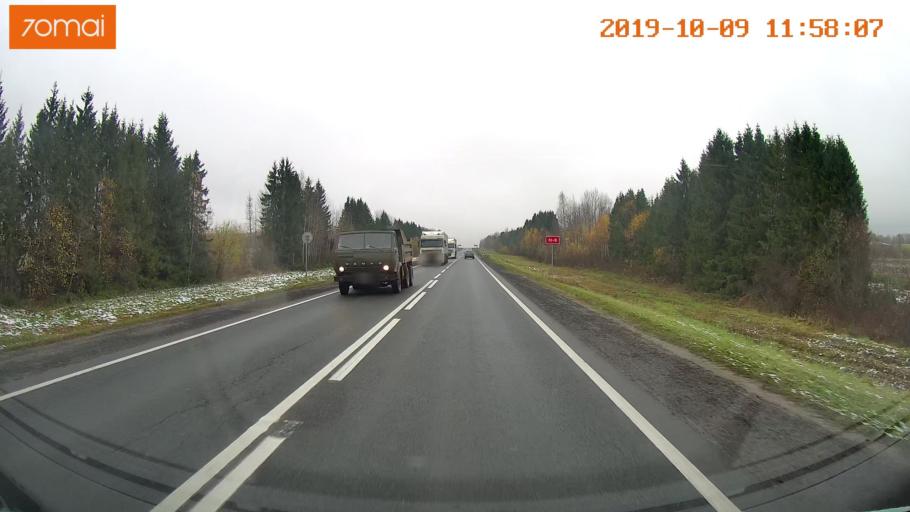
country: RU
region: Vologda
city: Gryazovets
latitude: 58.7227
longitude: 40.2960
